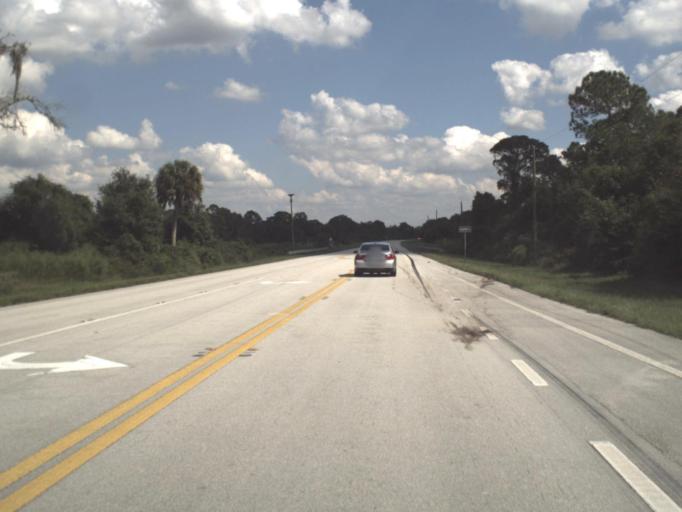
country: US
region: Florida
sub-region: Highlands County
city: Lake Placid
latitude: 27.3814
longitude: -81.1168
